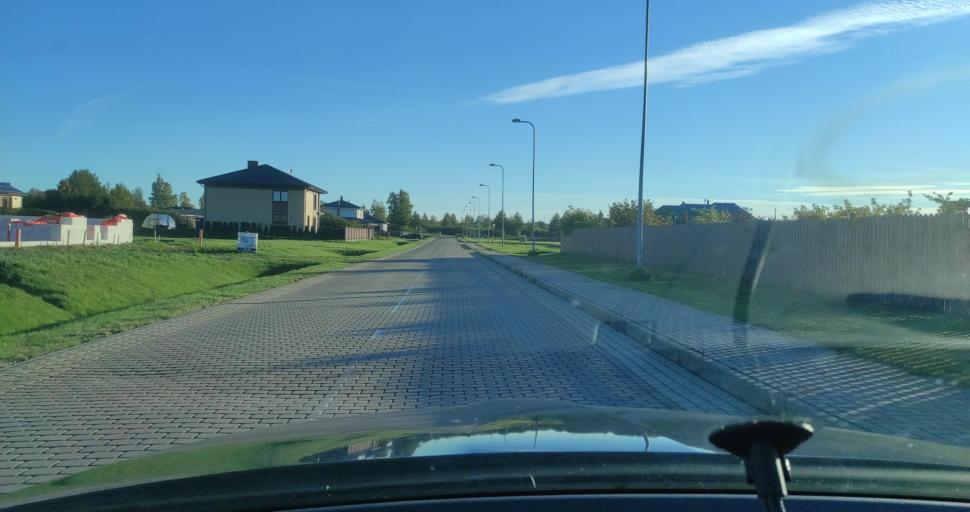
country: LV
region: Ventspils
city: Ventspils
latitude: 57.3676
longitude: 21.5742
